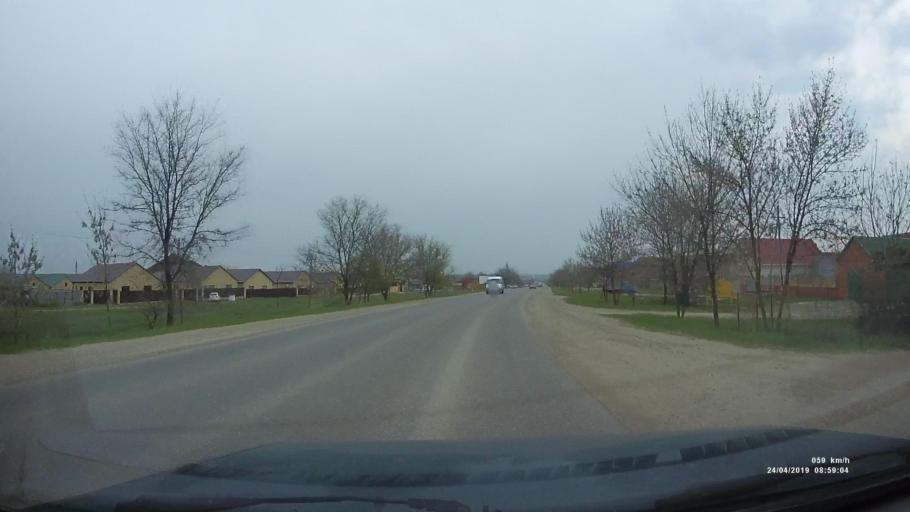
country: RU
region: Kalmykiya
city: Arshan'
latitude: 46.3121
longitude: 44.2043
